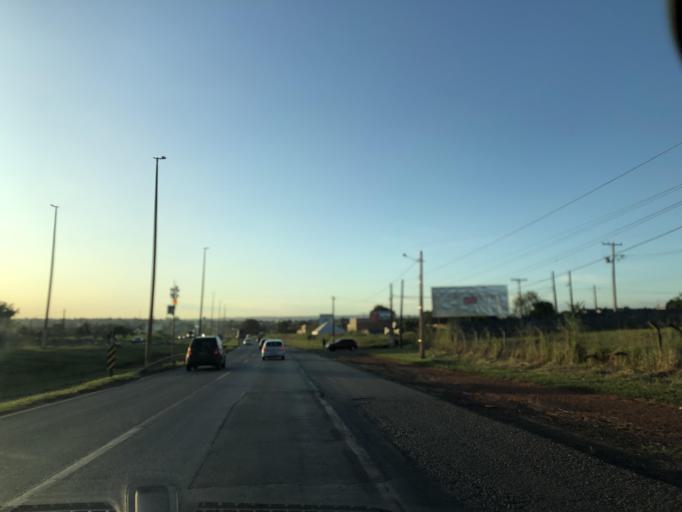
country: BR
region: Goias
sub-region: Luziania
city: Luziania
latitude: -16.1593
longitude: -47.9325
